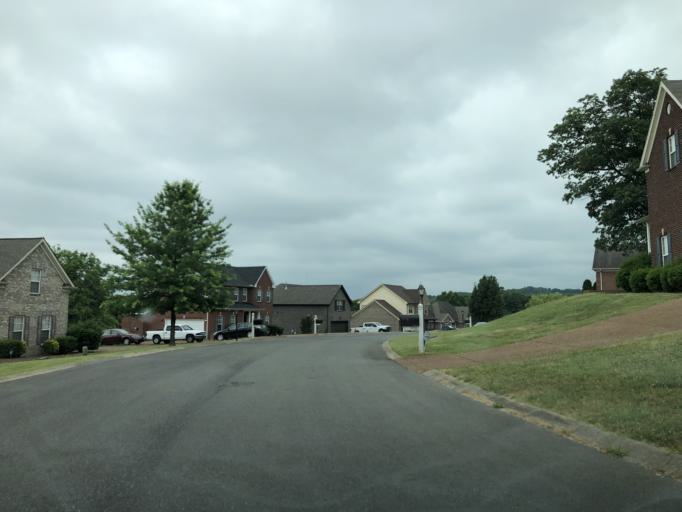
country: US
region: Tennessee
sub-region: Davidson County
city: Goodlettsville
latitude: 36.2939
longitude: -86.7359
